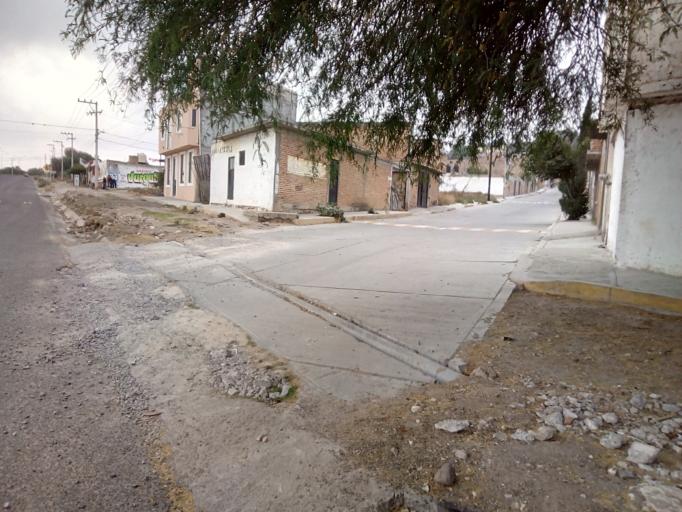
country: MX
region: Guerrero
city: San Luis de la Paz
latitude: 21.2830
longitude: -100.5035
